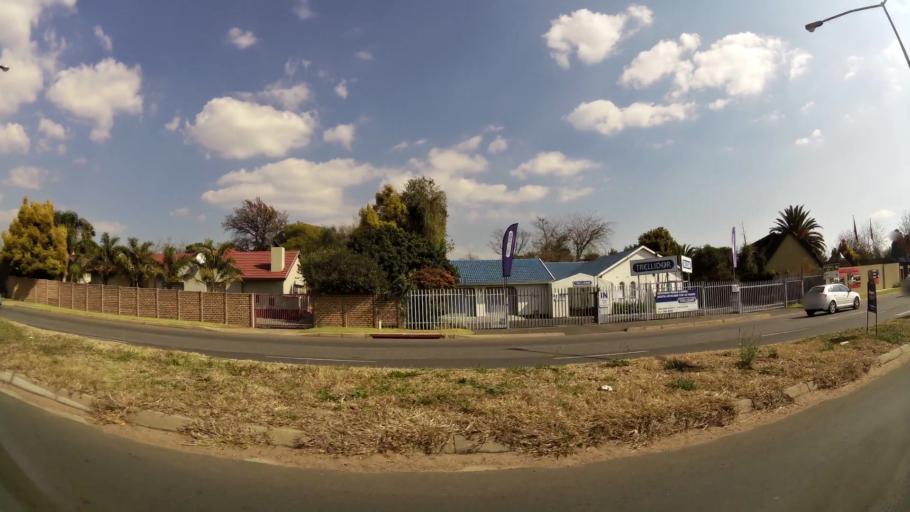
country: ZA
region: Gauteng
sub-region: City of Johannesburg Metropolitan Municipality
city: Modderfontein
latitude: -26.0879
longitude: 28.2498
